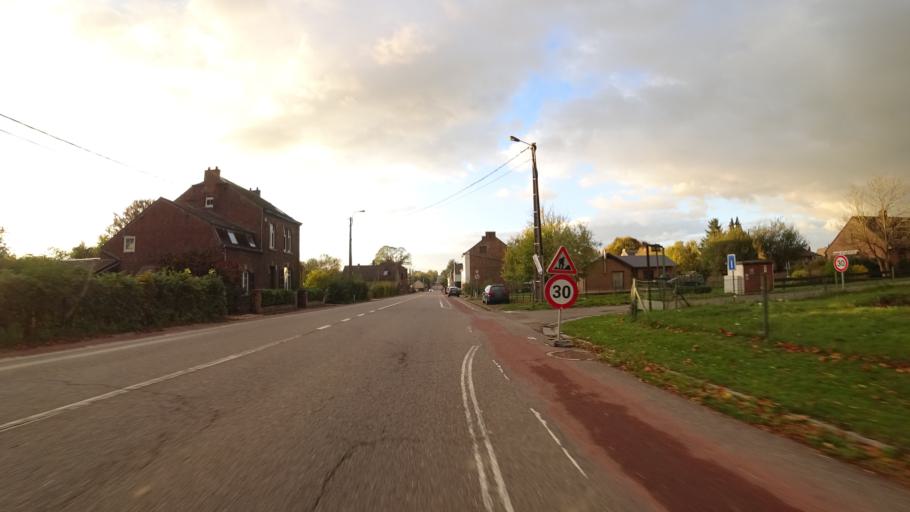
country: BE
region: Wallonia
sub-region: Province de Namur
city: Namur
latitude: 50.4970
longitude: 4.8004
